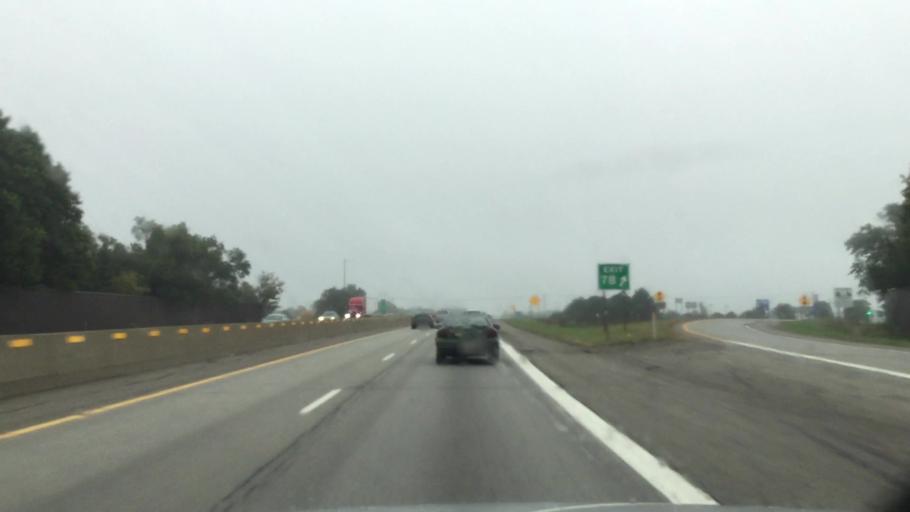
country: US
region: Michigan
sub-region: Kalamazoo County
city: Portage
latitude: 42.2435
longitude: -85.5641
